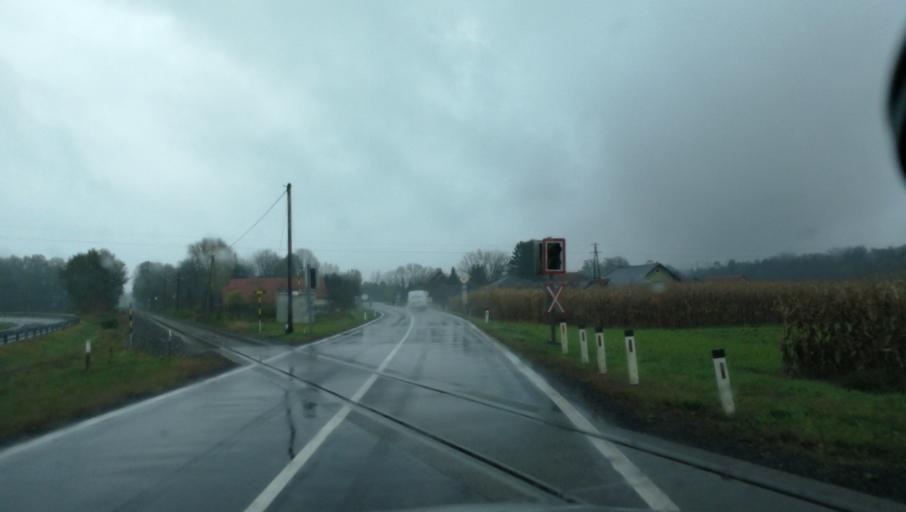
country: AT
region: Styria
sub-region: Politischer Bezirk Leibnitz
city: Spielfeld
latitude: 46.7179
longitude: 15.6610
